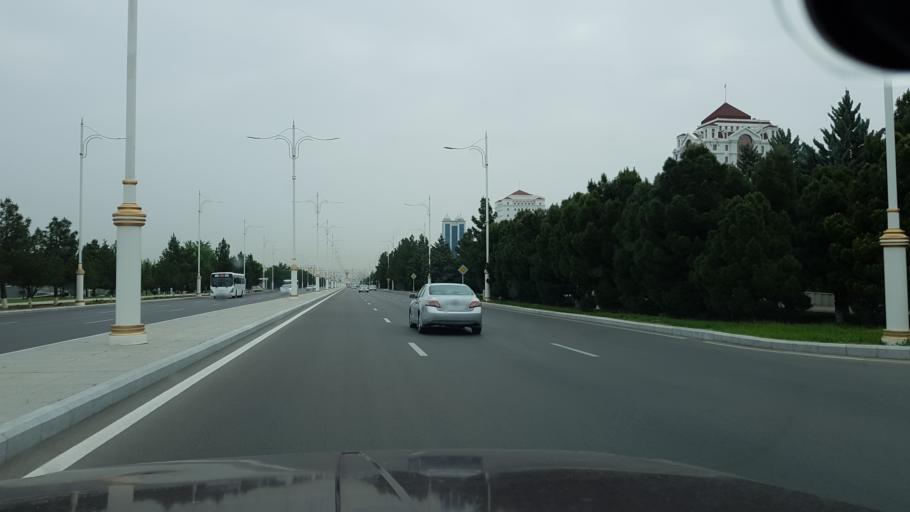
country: TM
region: Ahal
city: Ashgabat
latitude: 37.8861
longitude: 58.3877
